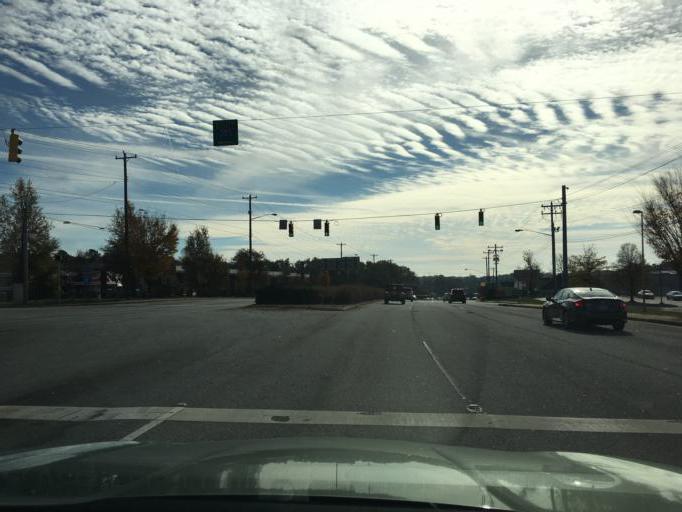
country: US
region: South Carolina
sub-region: Greenville County
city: Greenville
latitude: 34.8572
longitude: -82.3564
